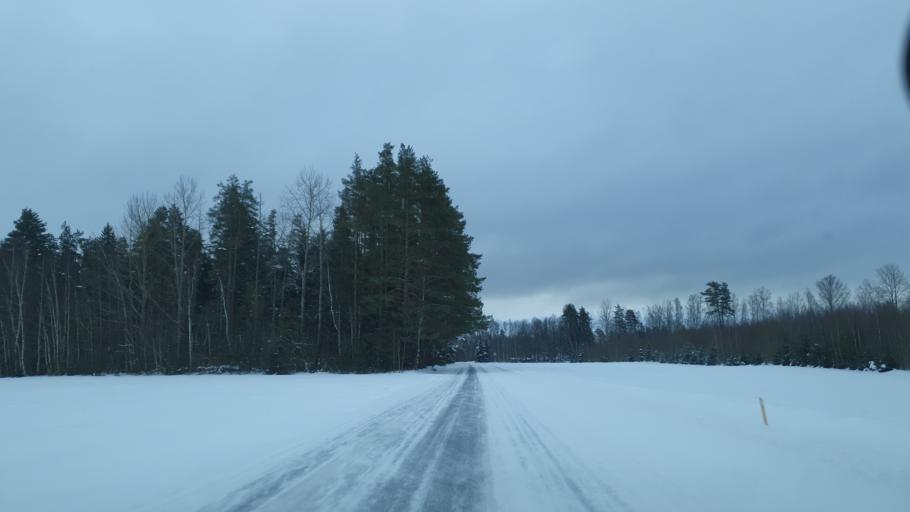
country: EE
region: Polvamaa
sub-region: Polva linn
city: Polva
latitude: 58.1285
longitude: 27.0900
